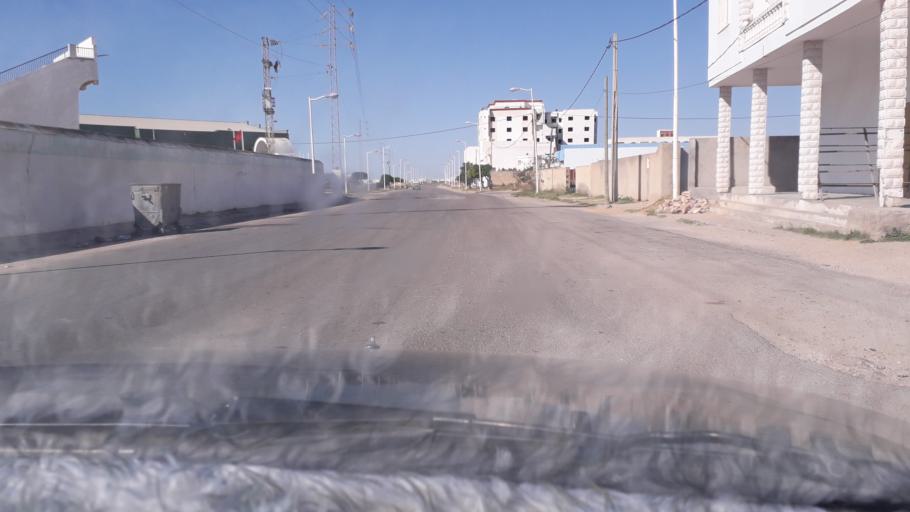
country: TN
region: Safaqis
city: Al Qarmadah
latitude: 34.8441
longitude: 10.7578
